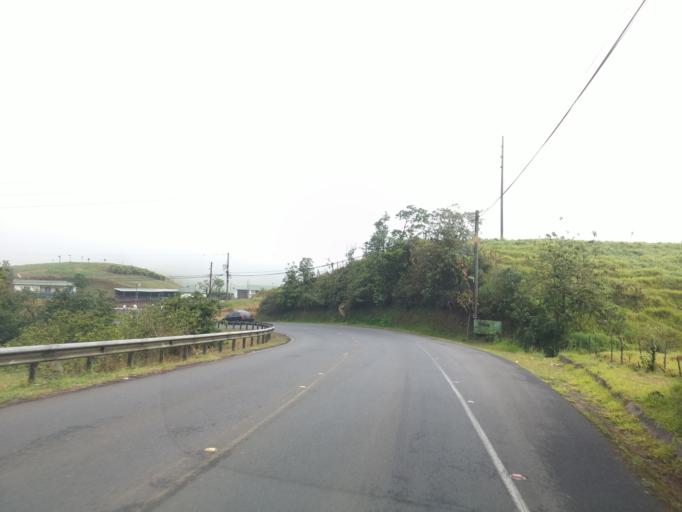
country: CR
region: Alajuela
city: San Ramon
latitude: 10.1538
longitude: -84.4929
